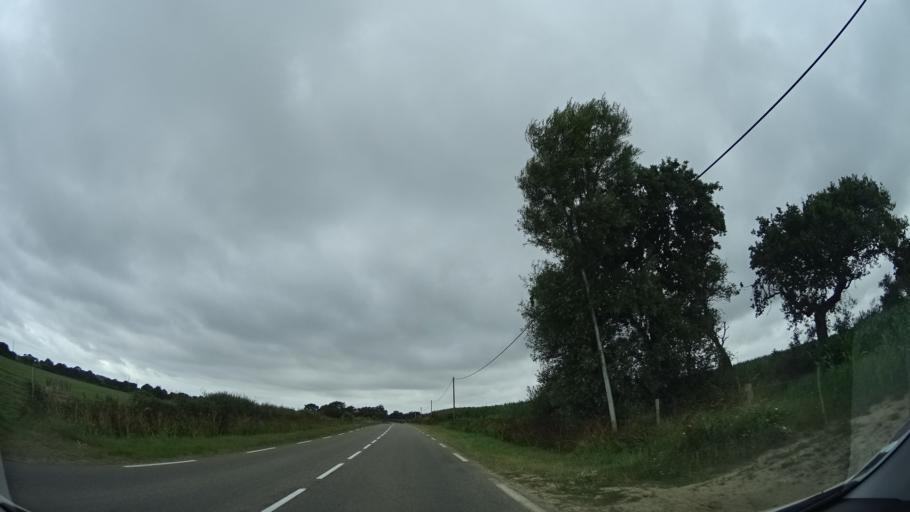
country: FR
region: Lower Normandy
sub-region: Departement de la Manche
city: La Haye-du-Puits
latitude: 49.3088
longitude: -1.5964
